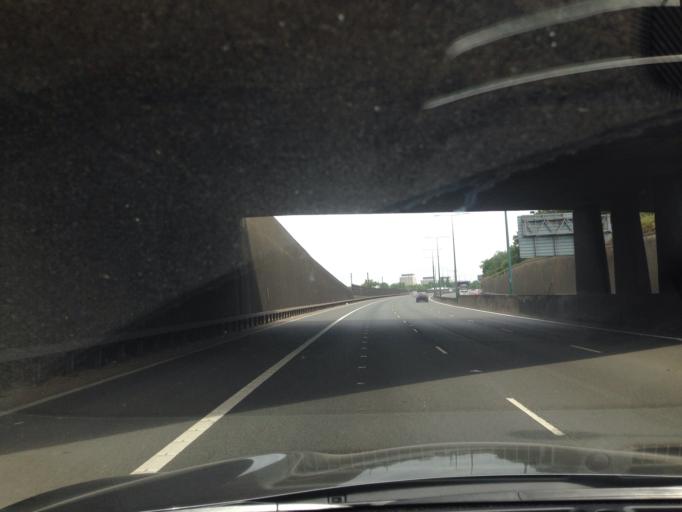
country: GB
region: England
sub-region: Greater London
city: Hendon
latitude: 51.5795
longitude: -0.2382
